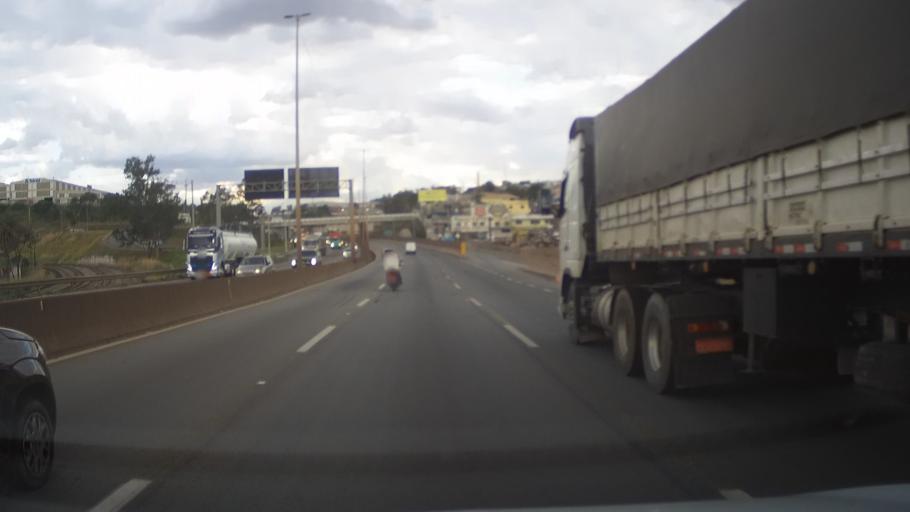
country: BR
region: Minas Gerais
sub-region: Betim
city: Betim
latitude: -19.9566
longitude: -44.1403
